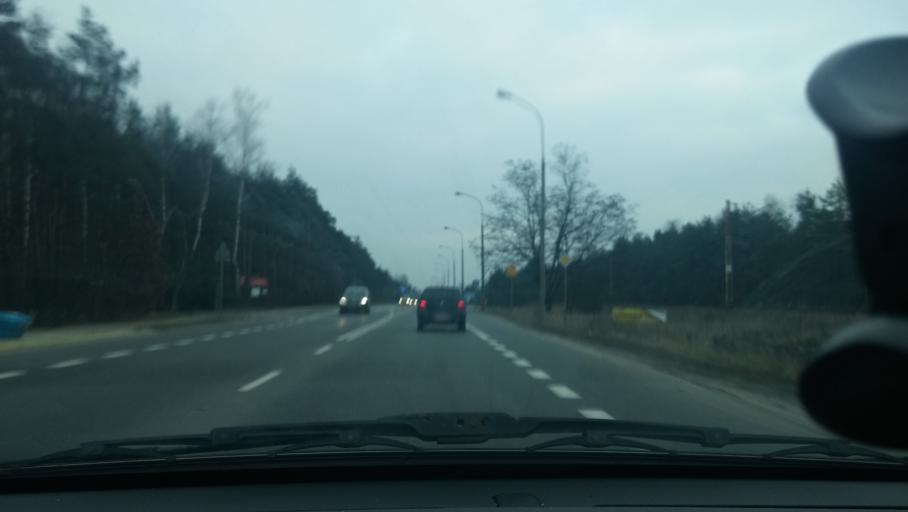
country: PL
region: Masovian Voivodeship
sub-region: Warszawa
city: Wawer
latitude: 52.1986
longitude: 21.1748
